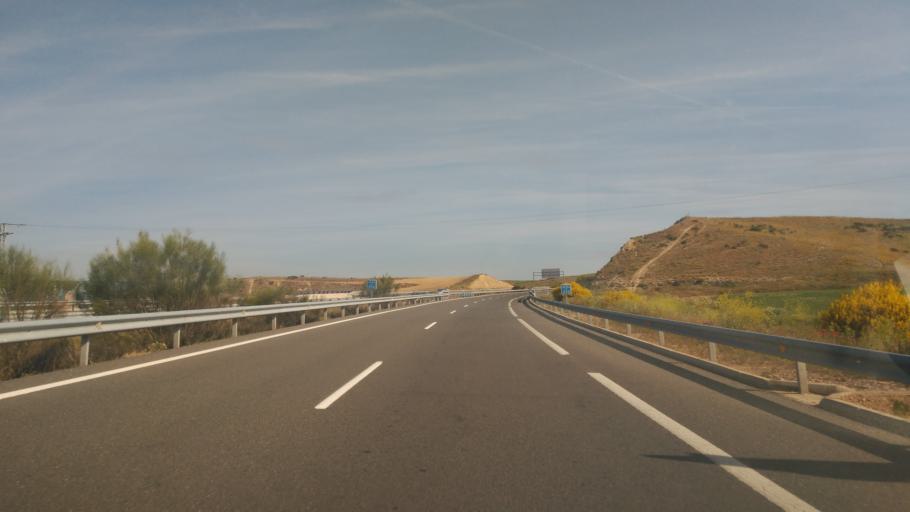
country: ES
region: Castille and Leon
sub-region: Provincia de Salamanca
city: Villamayor
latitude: 41.0031
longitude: -5.6779
